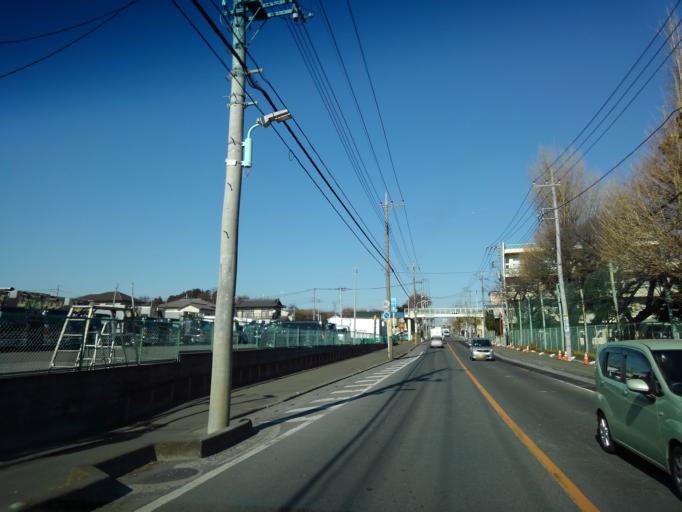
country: JP
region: Saitama
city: Oi
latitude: 35.8053
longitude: 139.5219
